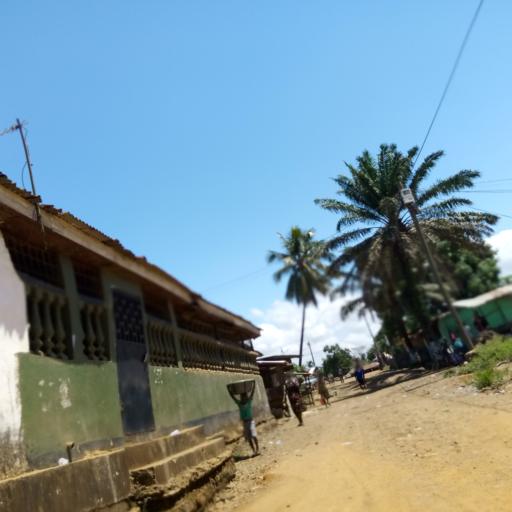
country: LR
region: Montserrado
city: Monrovia
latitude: 6.2403
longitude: -10.6946
